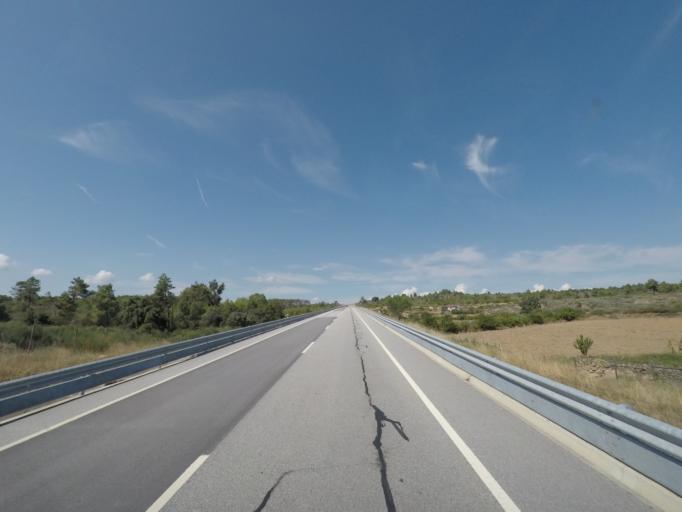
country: PT
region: Braganca
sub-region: Braganca Municipality
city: Vila Flor
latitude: 41.3001
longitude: -7.1690
